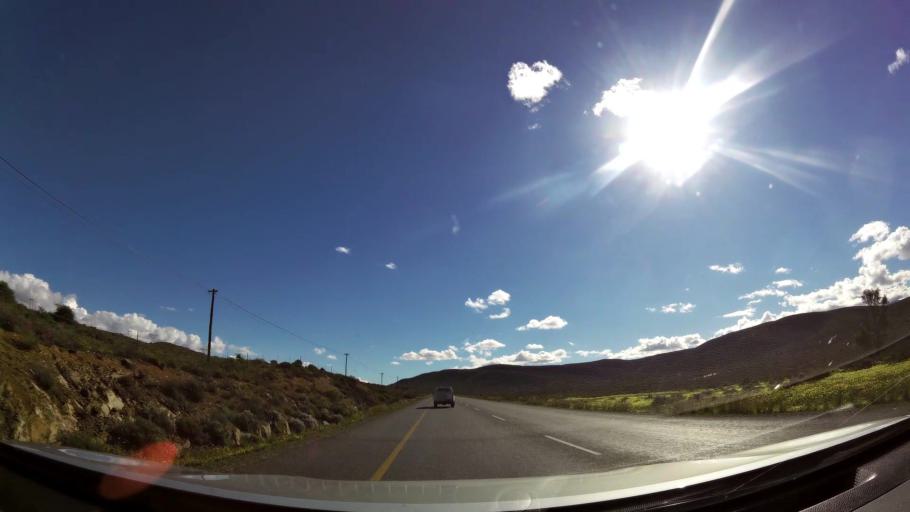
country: ZA
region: Western Cape
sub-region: Cape Winelands District Municipality
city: Worcester
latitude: -33.7365
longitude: 19.6767
